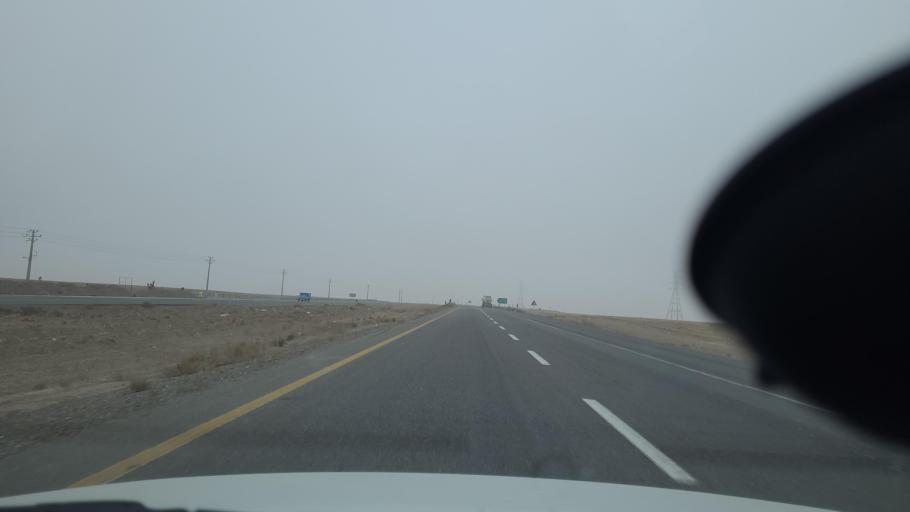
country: IR
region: Razavi Khorasan
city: Fariman
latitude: 35.8718
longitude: 59.7616
